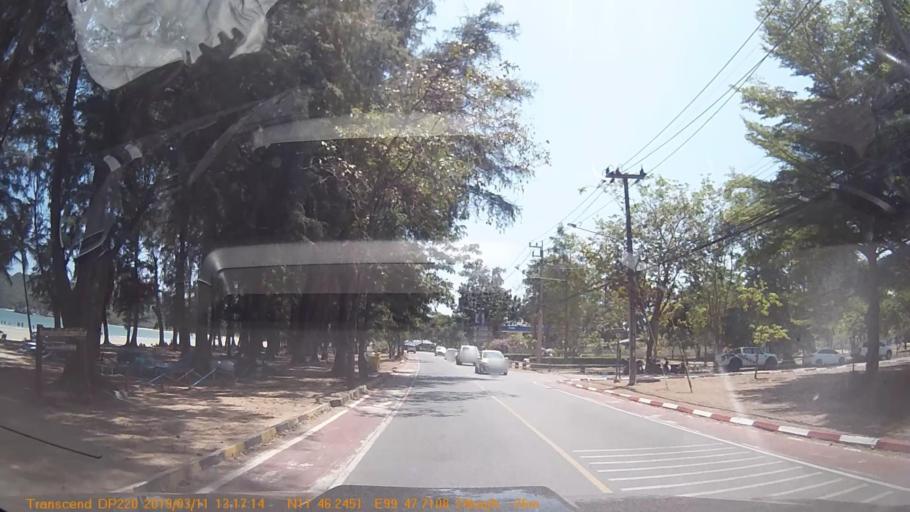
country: TH
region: Prachuap Khiri Khan
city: Prachuap Khiri Khan
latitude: 11.7707
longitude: 99.7952
